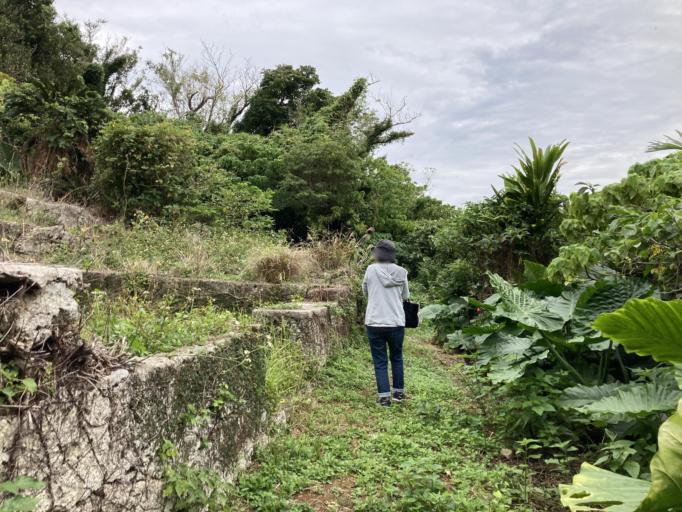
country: JP
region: Okinawa
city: Ishikawa
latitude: 26.3926
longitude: 127.7595
